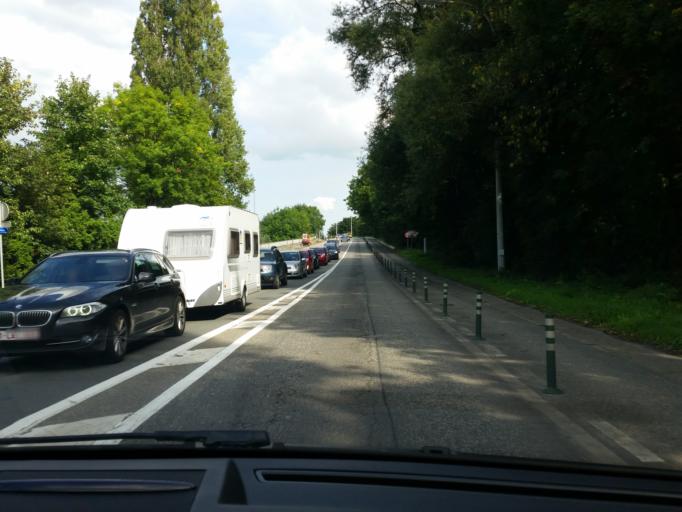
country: BE
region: Flanders
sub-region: Provincie Antwerpen
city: Mortsel
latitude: 51.1769
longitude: 4.4607
